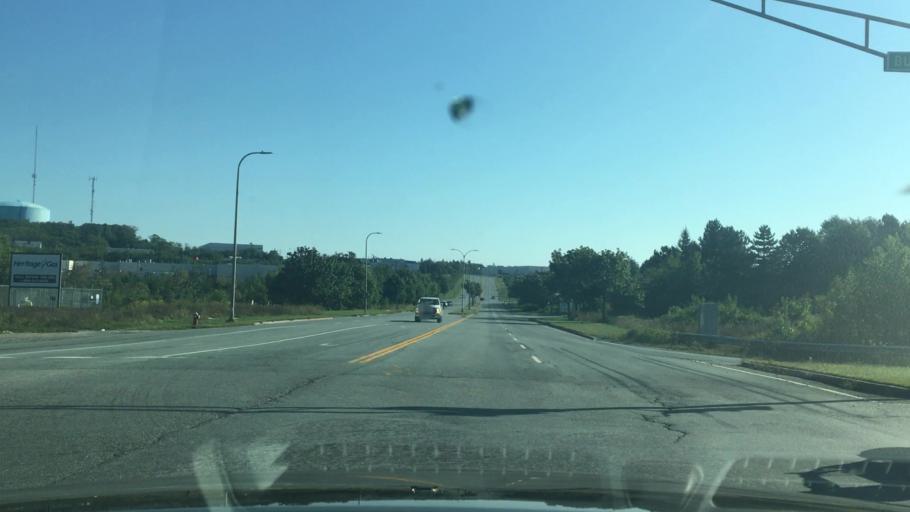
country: CA
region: Nova Scotia
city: Dartmouth
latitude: 44.7146
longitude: -63.5909
